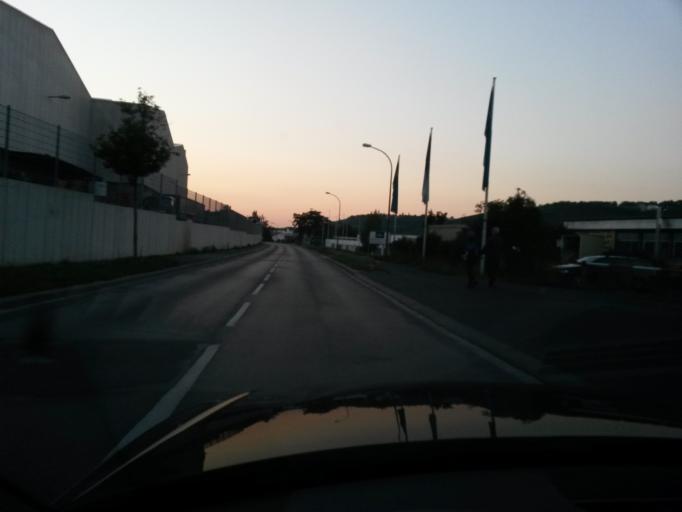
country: DE
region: Bavaria
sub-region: Regierungsbezirk Unterfranken
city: Randersacker
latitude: 49.7568
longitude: 9.9730
